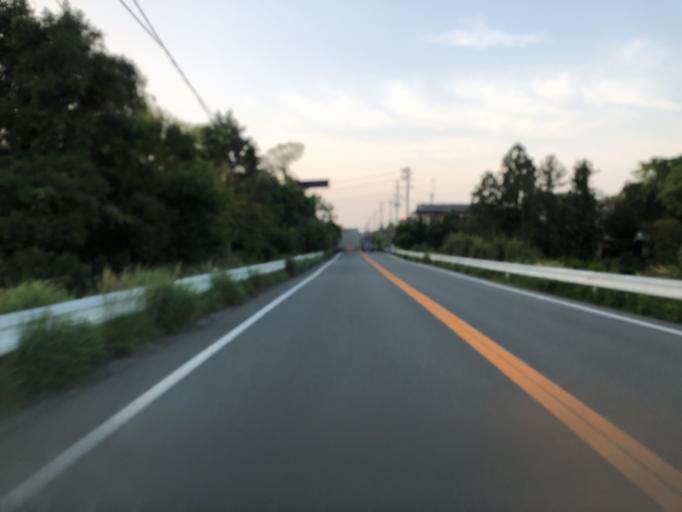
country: JP
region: Fukushima
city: Namie
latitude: 37.3806
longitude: 141.0087
